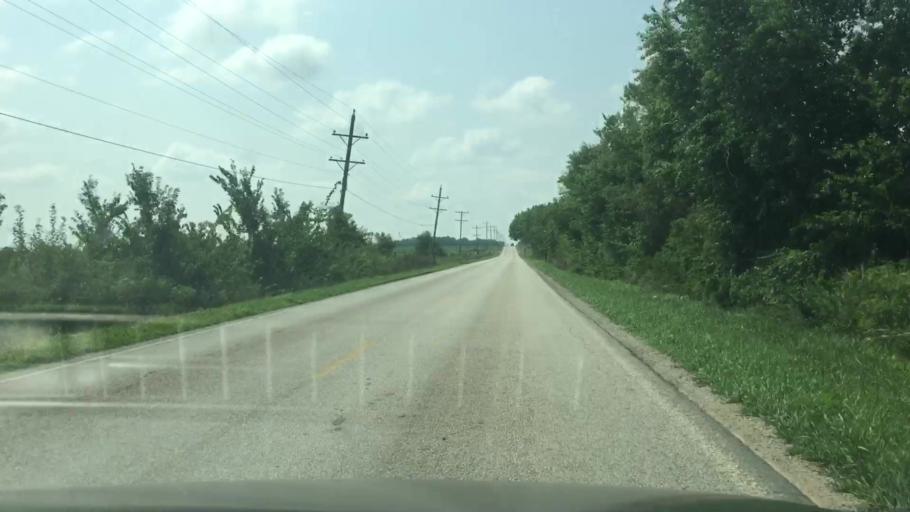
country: US
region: Kansas
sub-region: Allen County
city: Humboldt
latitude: 37.8527
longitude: -95.4369
